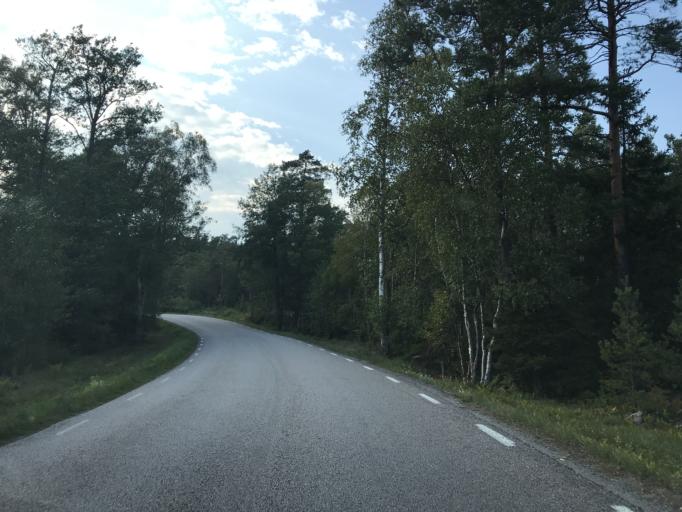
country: SE
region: Stockholm
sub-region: Norrtalje Kommun
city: Bjorko
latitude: 59.8687
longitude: 19.0238
